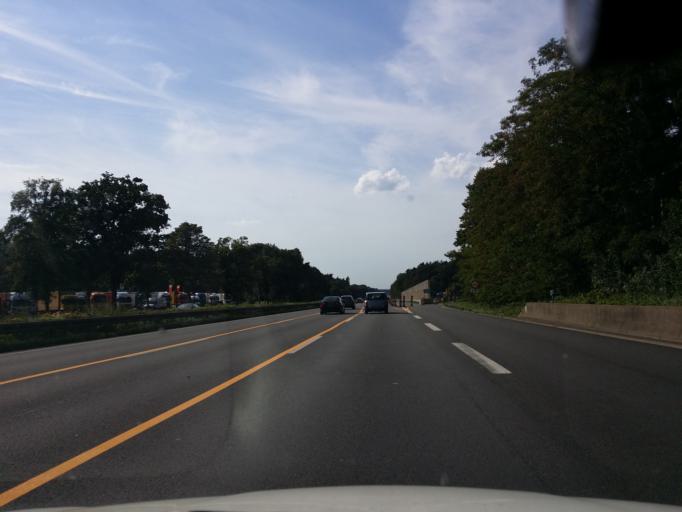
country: DE
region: North Rhine-Westphalia
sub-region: Regierungsbezirk Koln
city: Rosrath
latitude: 50.8978
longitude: 7.1553
